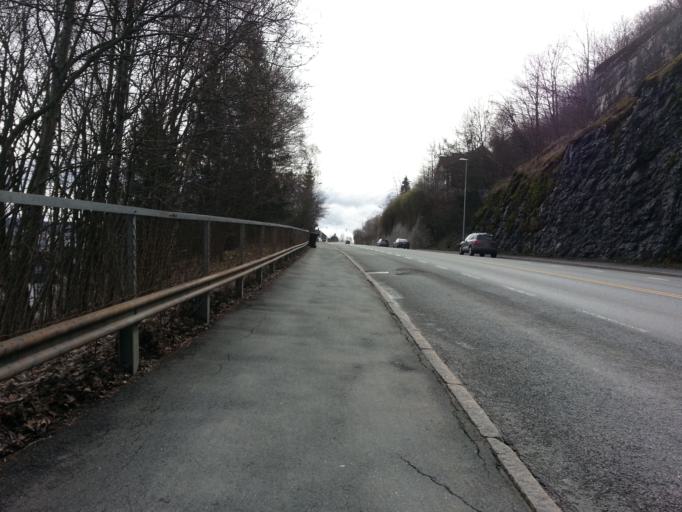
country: NO
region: Sor-Trondelag
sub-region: Trondheim
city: Trondheim
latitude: 63.4257
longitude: 10.3695
